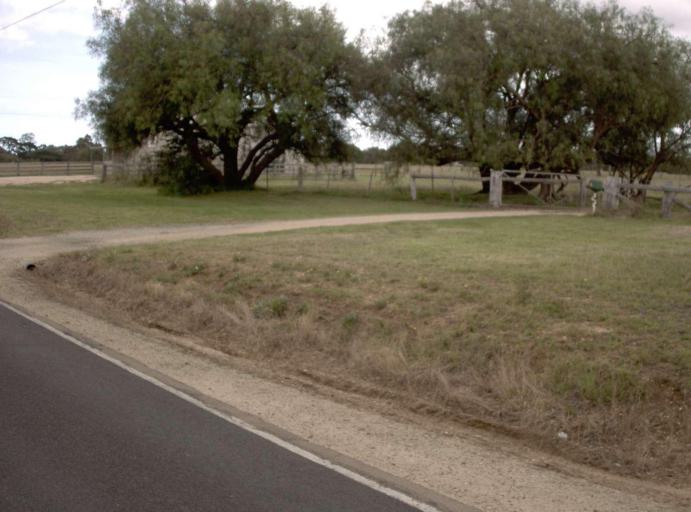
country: AU
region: Victoria
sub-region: Wellington
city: Sale
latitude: -38.1794
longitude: 147.0898
